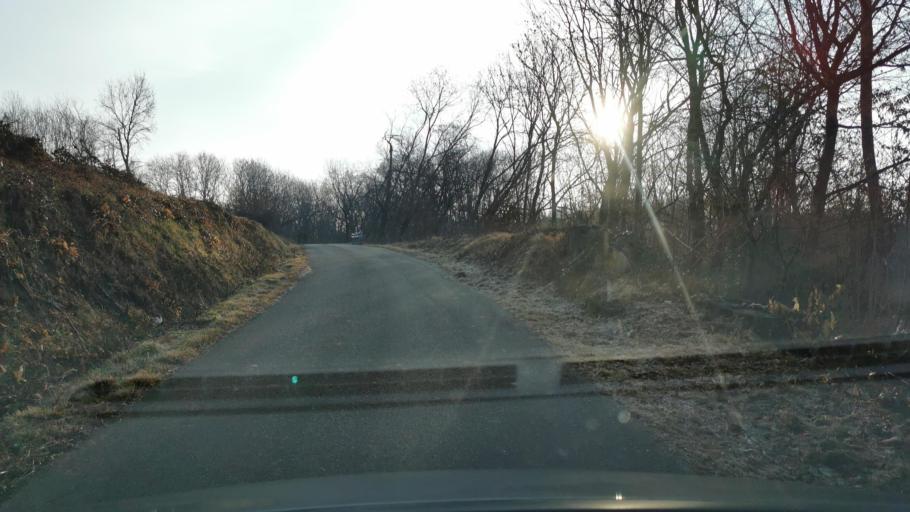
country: IT
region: Piedmont
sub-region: Provincia di Torino
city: Rocca Canavese
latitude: 45.2836
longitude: 7.5738
